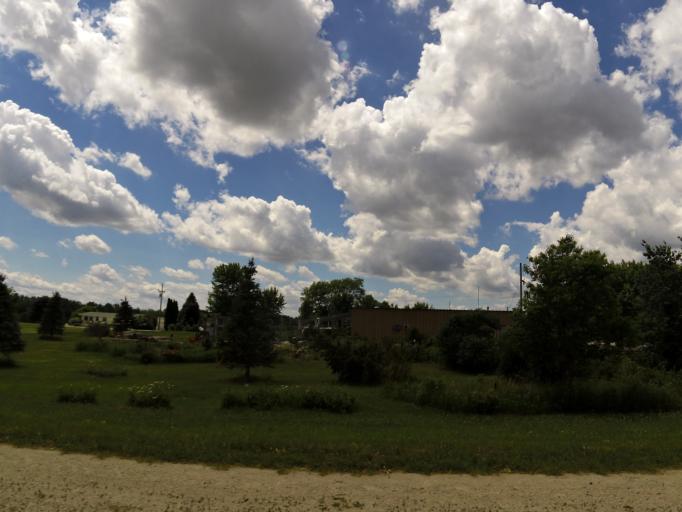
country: US
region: Iowa
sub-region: Fayette County
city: Oelwein
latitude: 42.6073
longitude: -91.9034
